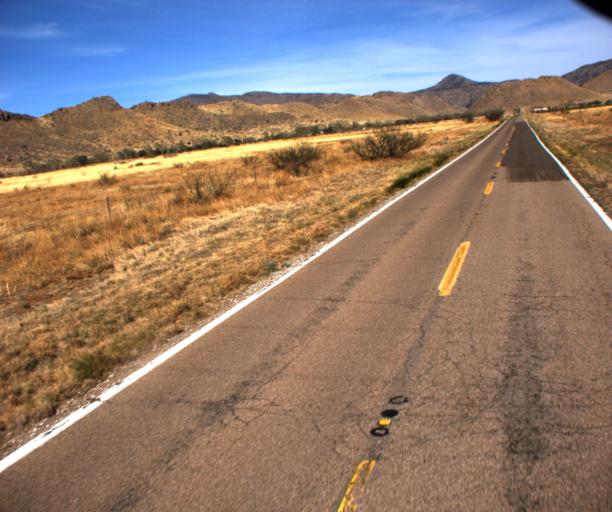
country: US
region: Arizona
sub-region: Cochise County
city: Willcox
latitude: 32.0067
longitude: -109.4170
